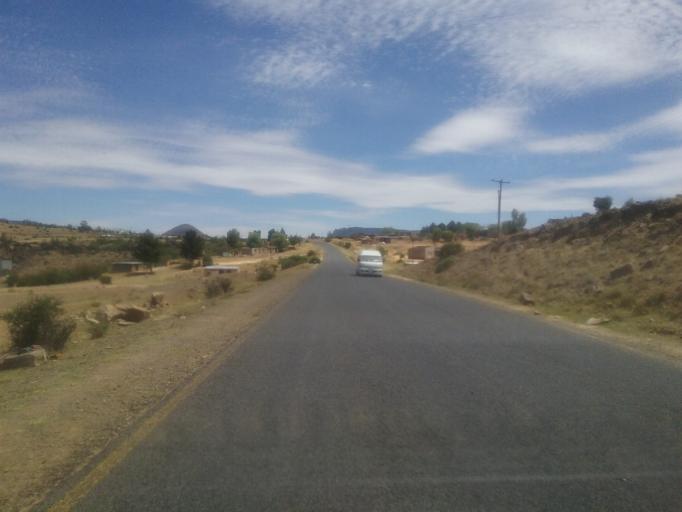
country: LS
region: Mafeteng
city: Mafeteng
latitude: -29.9942
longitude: 27.3366
